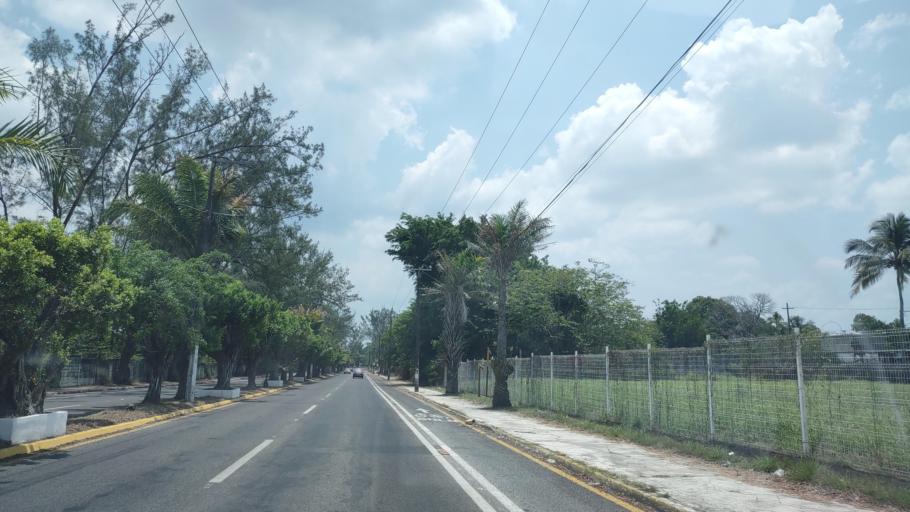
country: MX
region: Veracruz
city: Las Choapas
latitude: 17.9280
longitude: -94.0955
